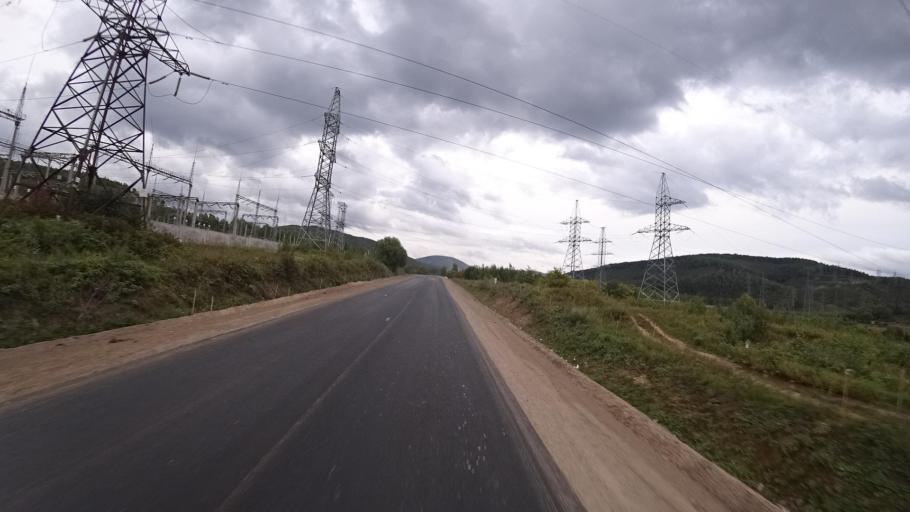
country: RU
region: Jewish Autonomous Oblast
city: Khingansk
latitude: 48.9906
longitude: 131.0924
